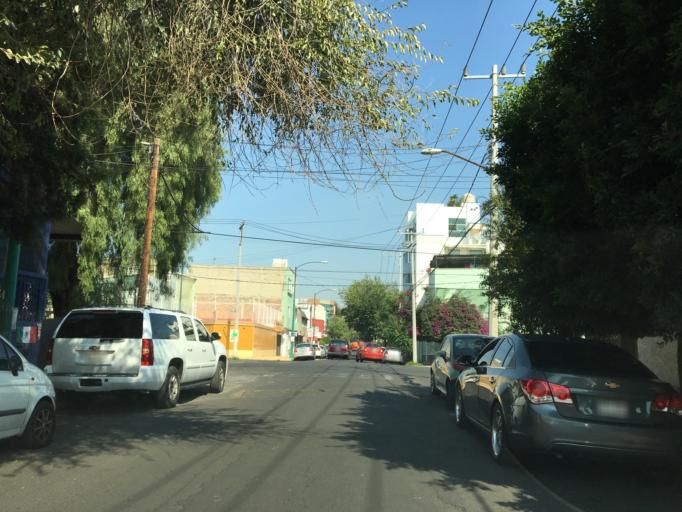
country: MX
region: Mexico
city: Colonia Lindavista
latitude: 19.4714
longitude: -99.1272
